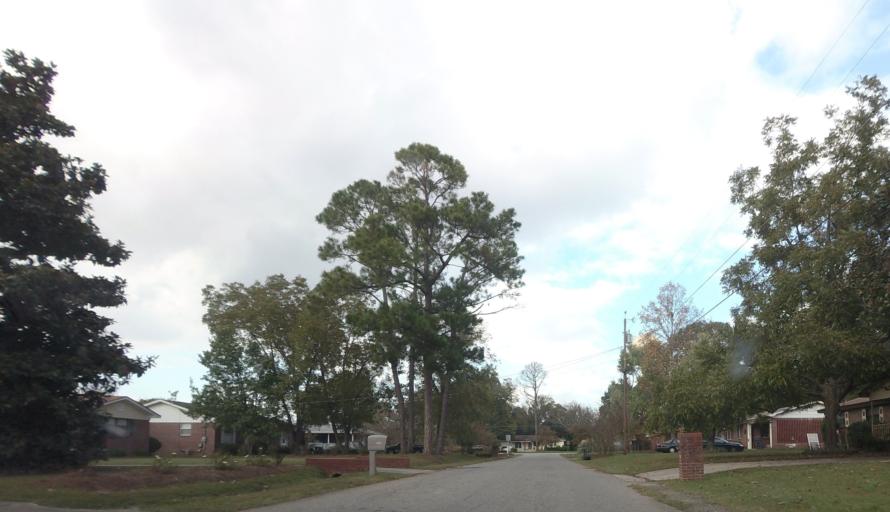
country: US
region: Georgia
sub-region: Houston County
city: Centerville
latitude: 32.6305
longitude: -83.6630
